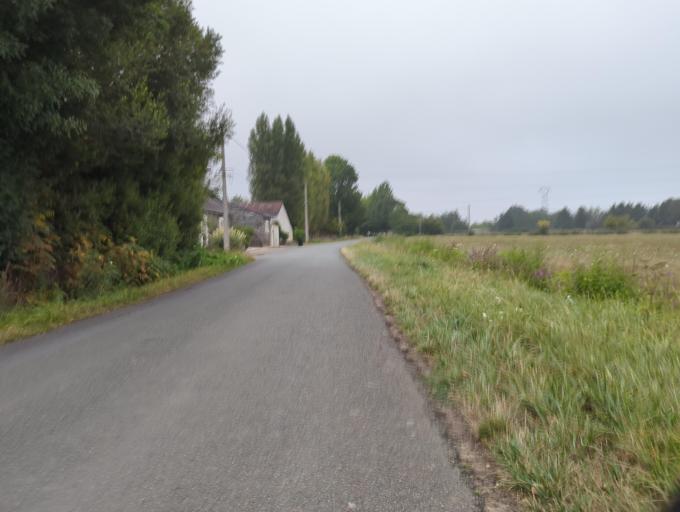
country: FR
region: Pays de la Loire
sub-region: Departement de Maine-et-Loire
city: Trelaze
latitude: 47.4777
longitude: -0.4587
